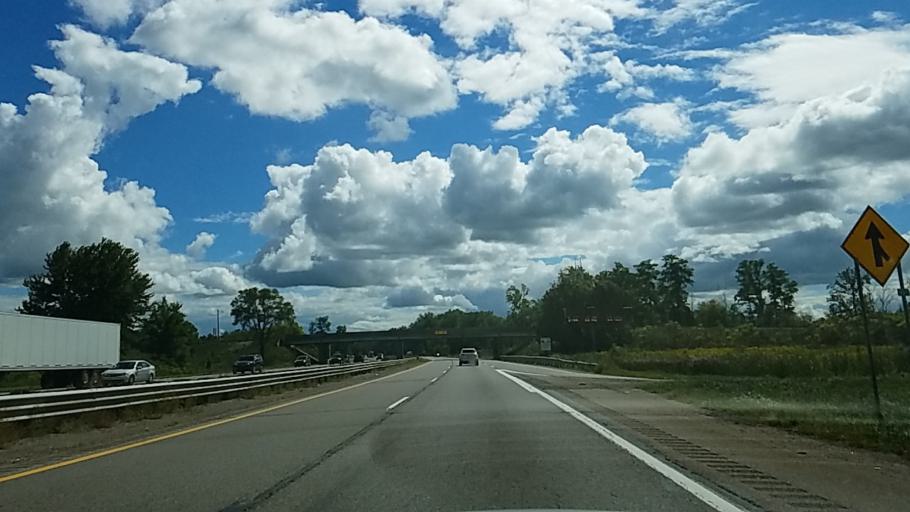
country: US
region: Michigan
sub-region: Livingston County
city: Whitmore Lake
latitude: 42.3961
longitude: -83.7637
